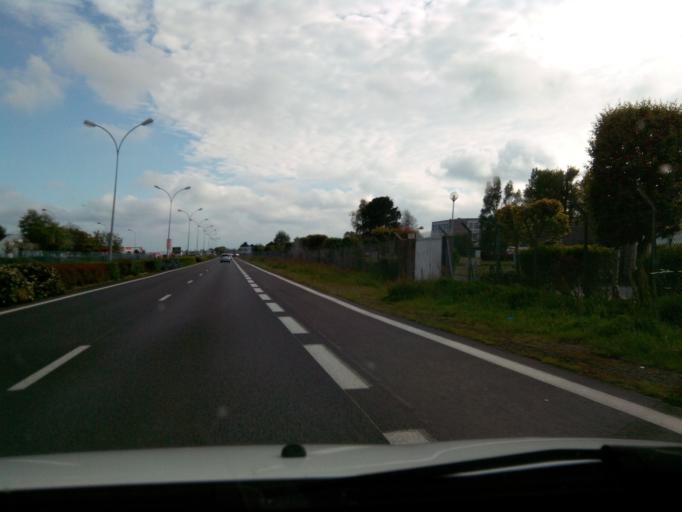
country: FR
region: Brittany
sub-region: Departement des Cotes-d'Armor
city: Lannion
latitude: 48.7566
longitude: -3.4553
